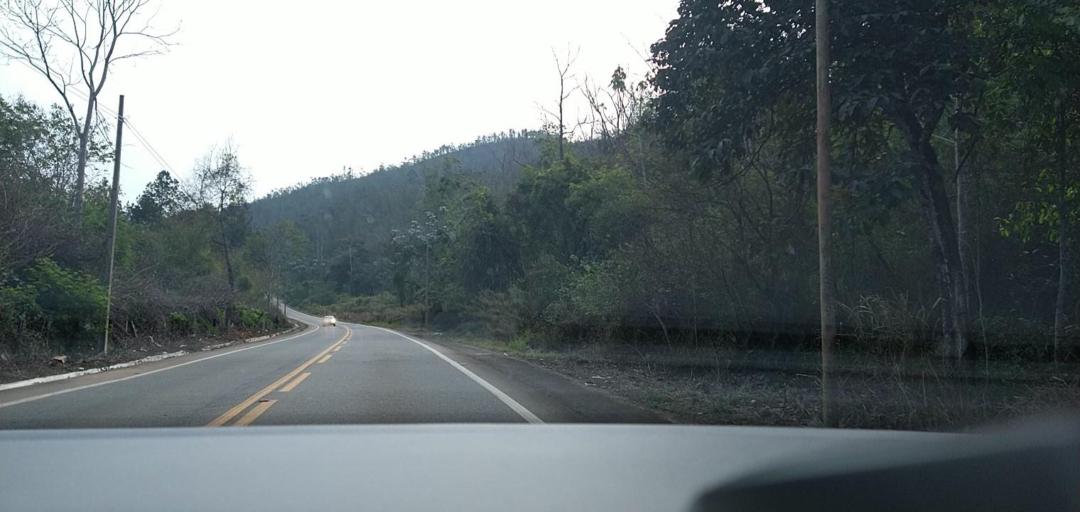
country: BR
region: Minas Gerais
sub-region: Rio Piracicaba
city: Rio Piracicaba
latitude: -19.8880
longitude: -43.1347
